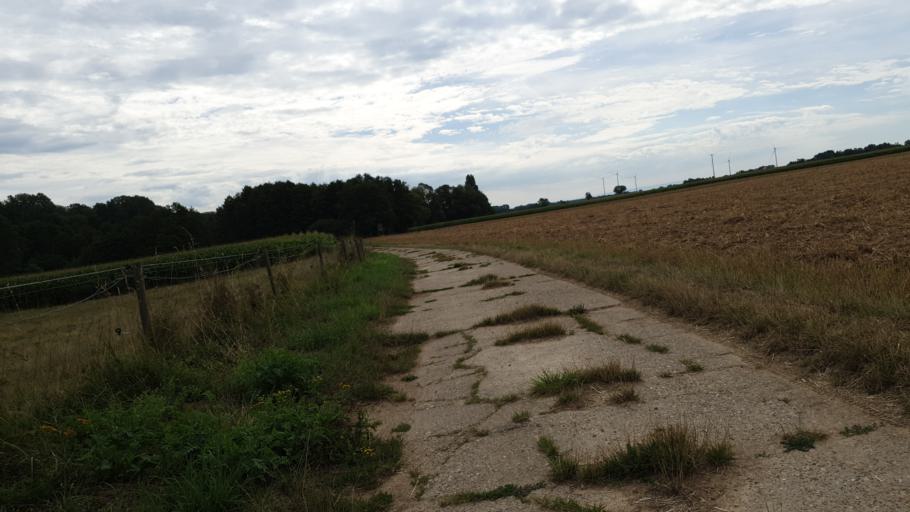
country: DE
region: Rheinland-Pfalz
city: Barbelroth
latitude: 49.1138
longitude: 8.0649
